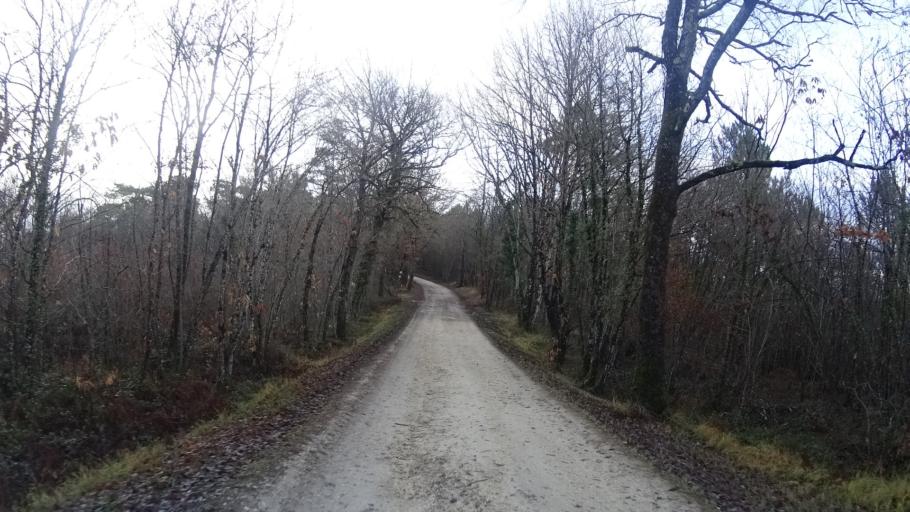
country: FR
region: Aquitaine
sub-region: Departement de la Dordogne
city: Antonne-et-Trigonant
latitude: 45.2083
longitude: 0.8669
